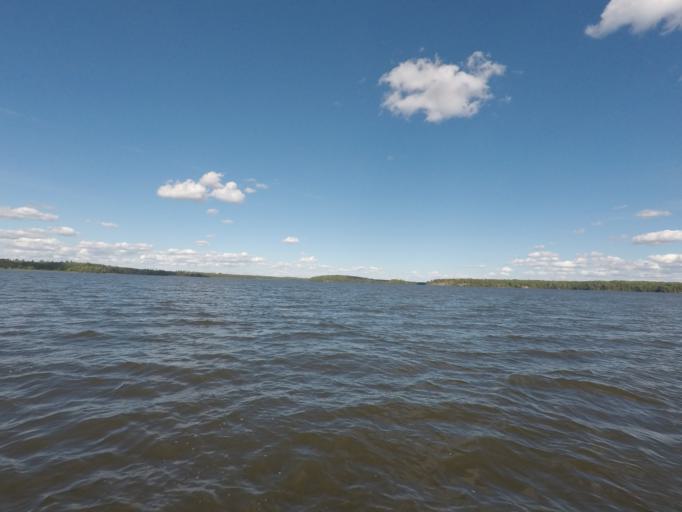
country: SE
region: Soedermanland
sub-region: Eskilstuna Kommun
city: Kvicksund
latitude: 59.4750
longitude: 16.3747
